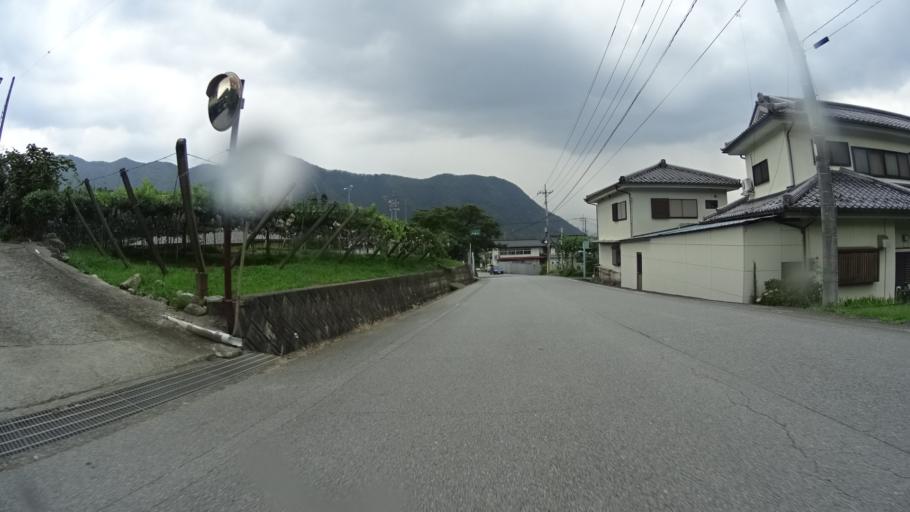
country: JP
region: Yamanashi
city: Enzan
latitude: 35.7506
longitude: 138.7155
